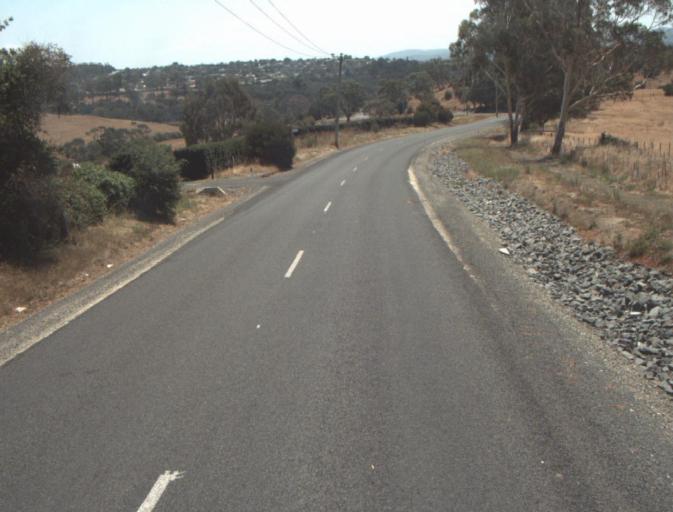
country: AU
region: Tasmania
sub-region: Launceston
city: Newstead
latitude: -41.4801
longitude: 147.1904
